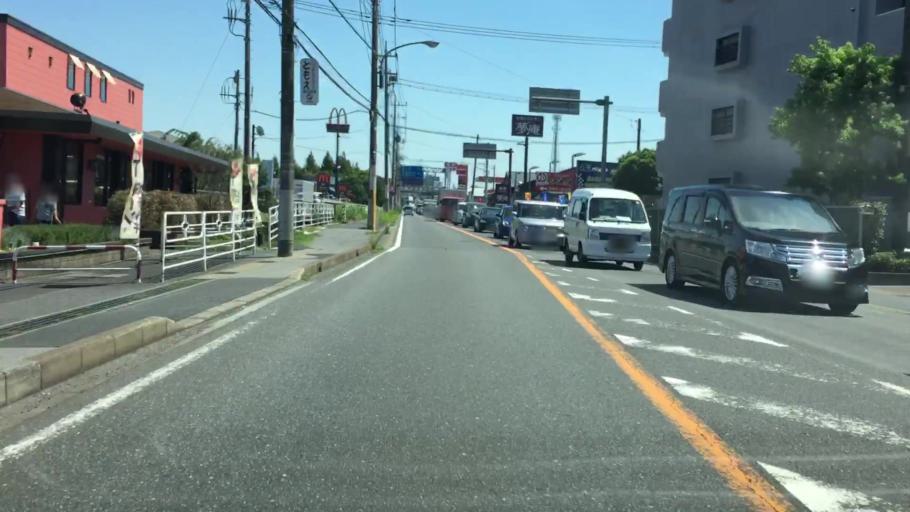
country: JP
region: Chiba
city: Funabashi
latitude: 35.7383
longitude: 139.9528
